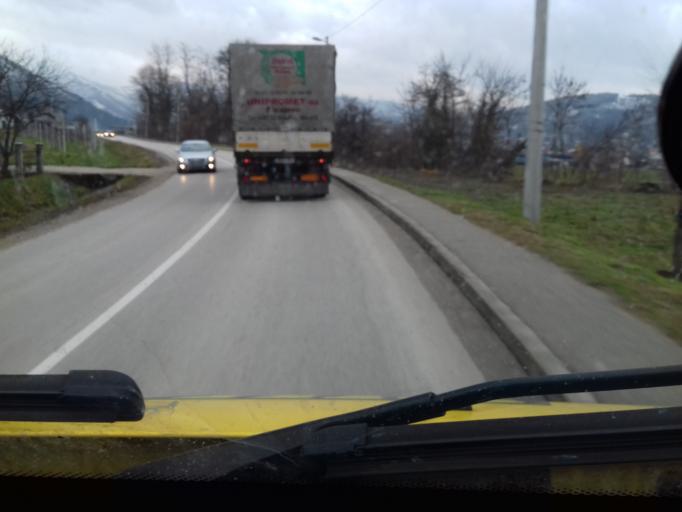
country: BA
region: Federation of Bosnia and Herzegovina
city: Zepce
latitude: 44.4233
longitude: 18.0484
